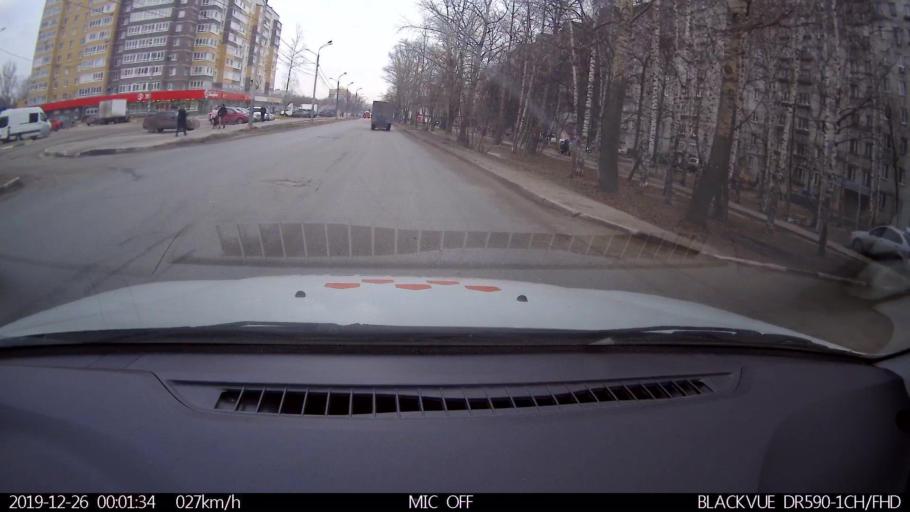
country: RU
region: Nizjnij Novgorod
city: Gorbatovka
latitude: 56.3417
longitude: 43.8297
